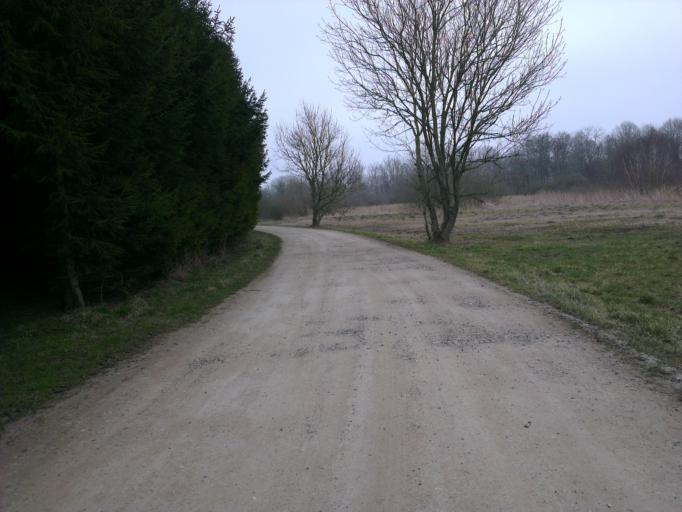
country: DK
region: Capital Region
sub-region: Frederikssund Kommune
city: Skibby
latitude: 55.7688
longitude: 12.0319
